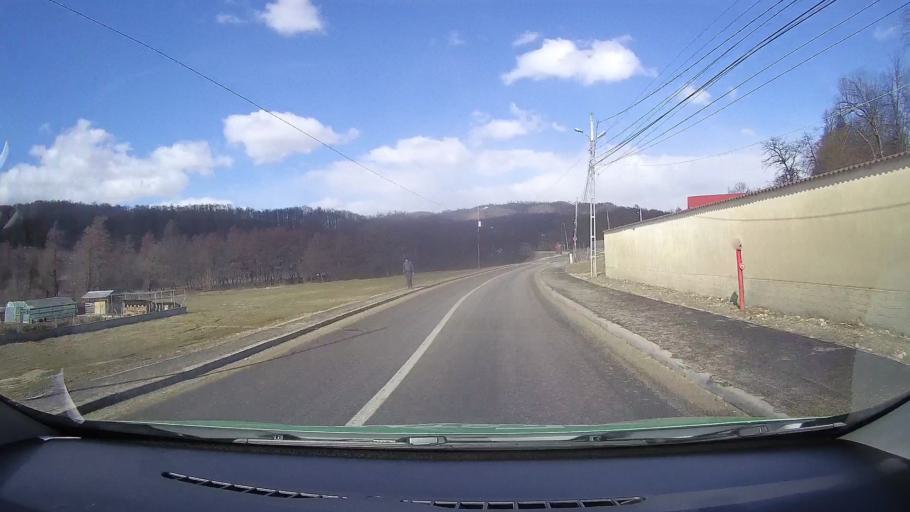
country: RO
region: Dambovita
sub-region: Comuna Fieni
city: Fieni
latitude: 45.1360
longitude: 25.4031
